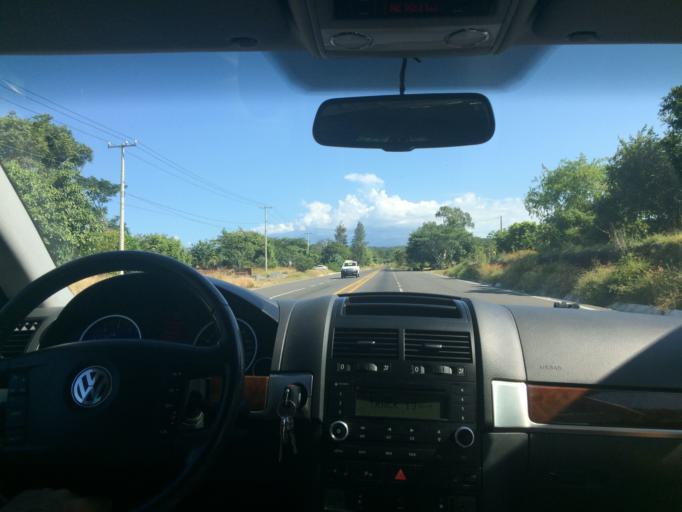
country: MX
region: Colima
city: Comala
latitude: 19.3440
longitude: -103.7411
